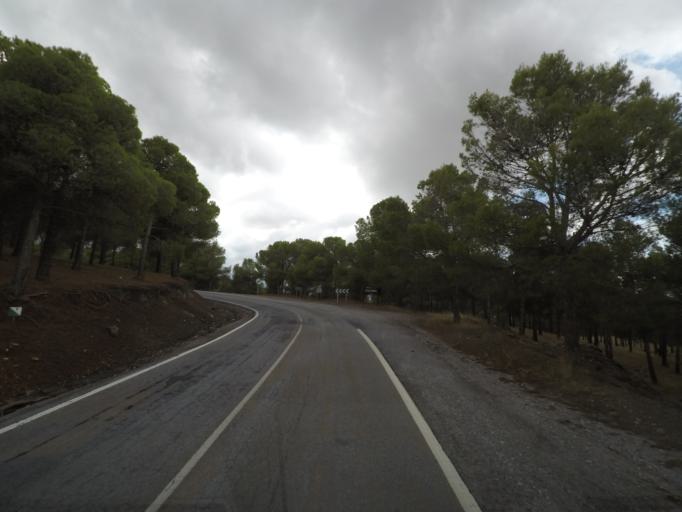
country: ES
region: Andalusia
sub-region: Provincia de Granada
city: Ferreira
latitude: 37.1743
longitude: -3.0484
